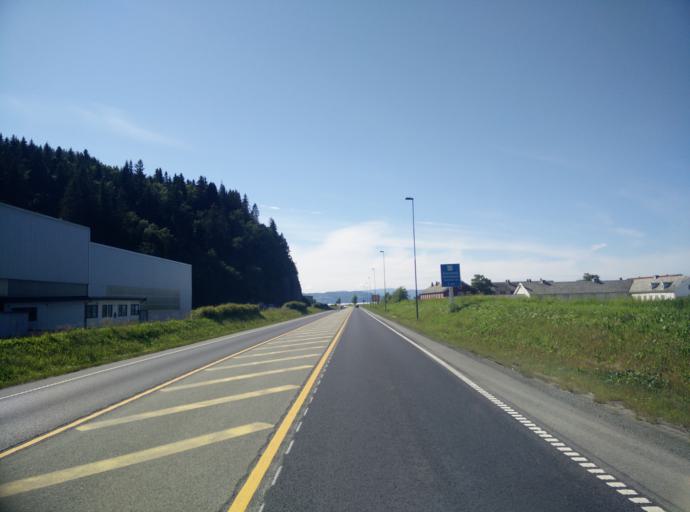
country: NO
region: Sor-Trondelag
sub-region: Melhus
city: Melhus
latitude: 63.3240
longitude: 10.2378
